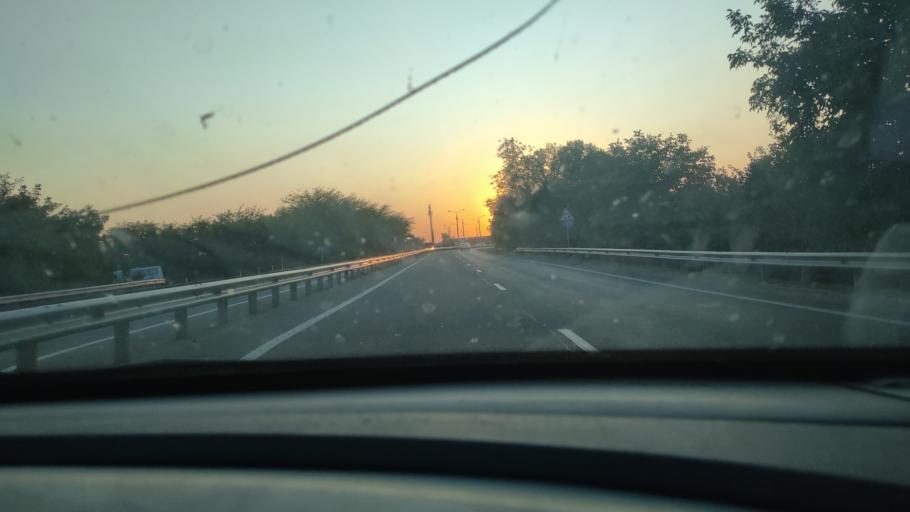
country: RU
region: Krasnodarskiy
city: Timashevsk
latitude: 45.5998
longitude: 38.9369
